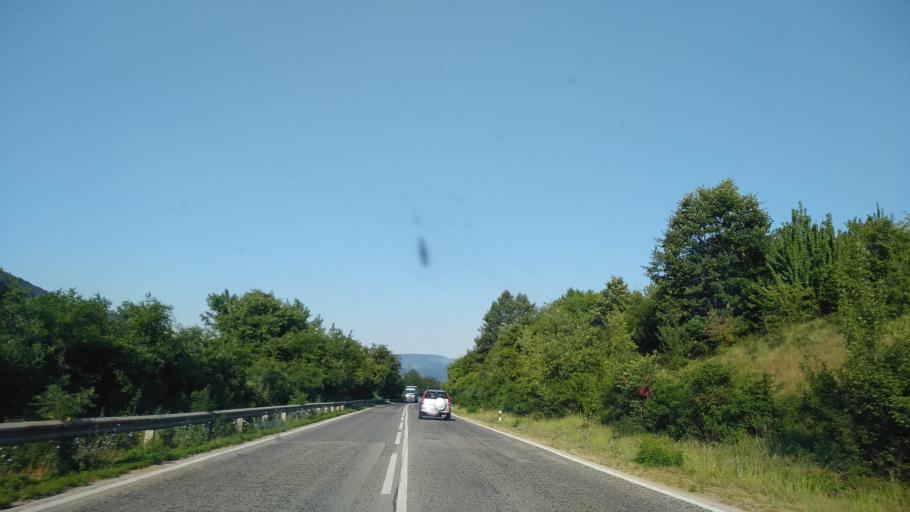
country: BG
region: Lovech
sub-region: Obshtina Lovech
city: Lovech
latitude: 43.0497
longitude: 24.8040
